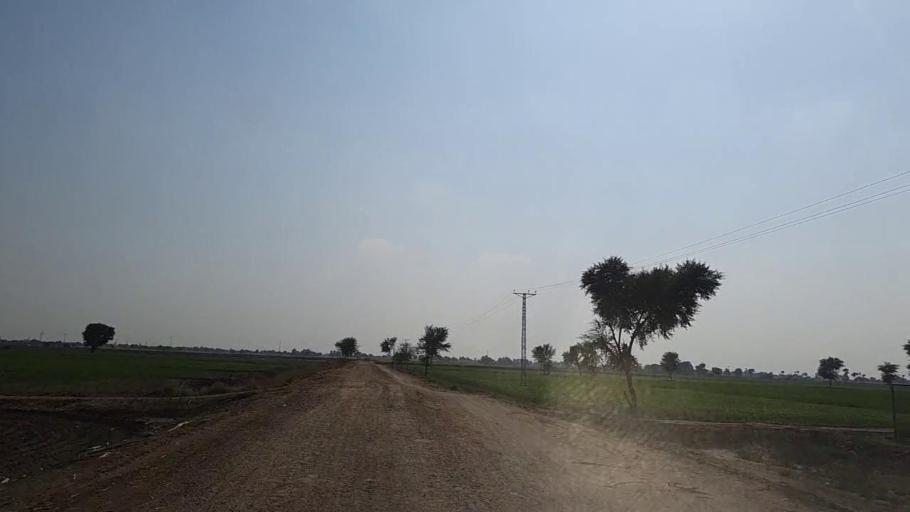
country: PK
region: Sindh
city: Daur
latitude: 26.4468
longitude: 68.2346
